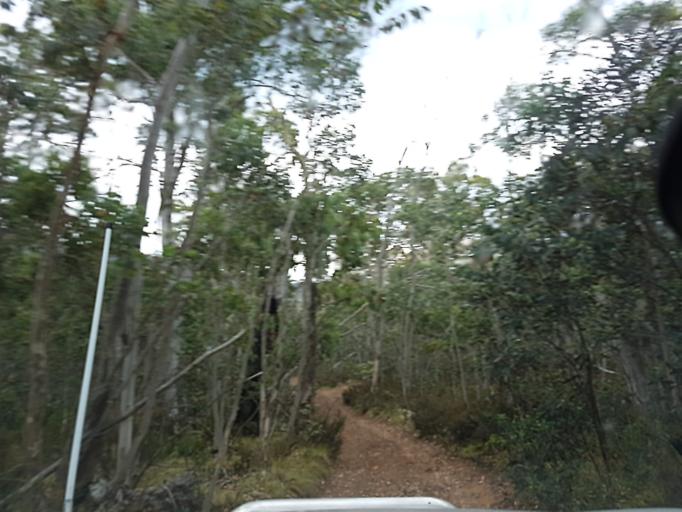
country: AU
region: New South Wales
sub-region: Snowy River
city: Jindabyne
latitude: -36.8789
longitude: 148.1595
